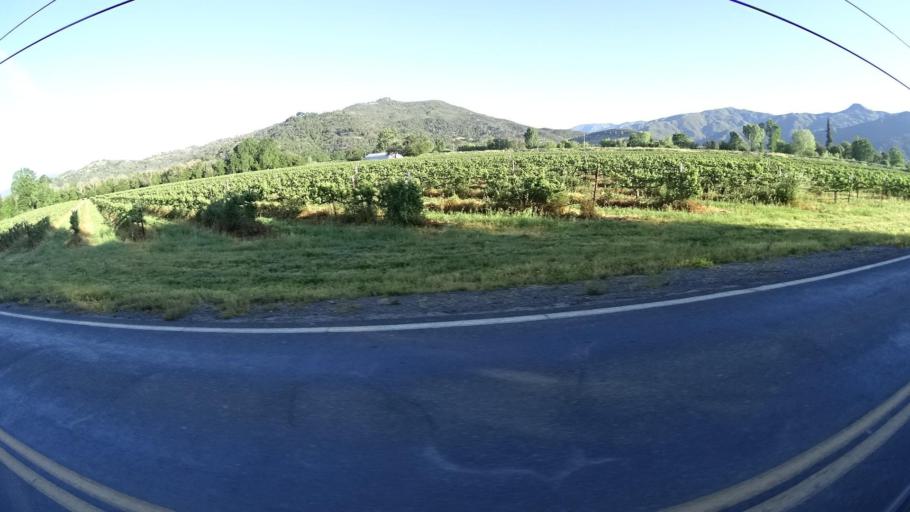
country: US
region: California
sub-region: Lake County
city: Upper Lake
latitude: 39.1733
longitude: -122.9041
